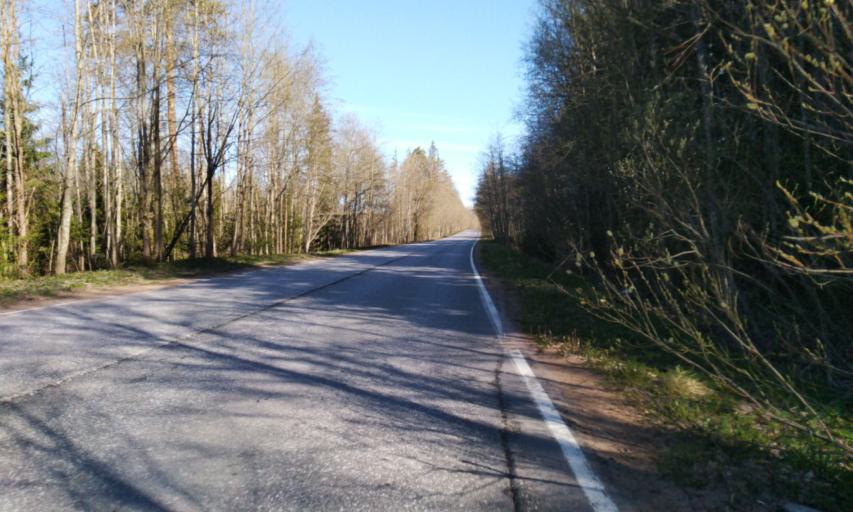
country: RU
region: Leningrad
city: Garbolovo
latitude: 60.3634
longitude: 30.4429
